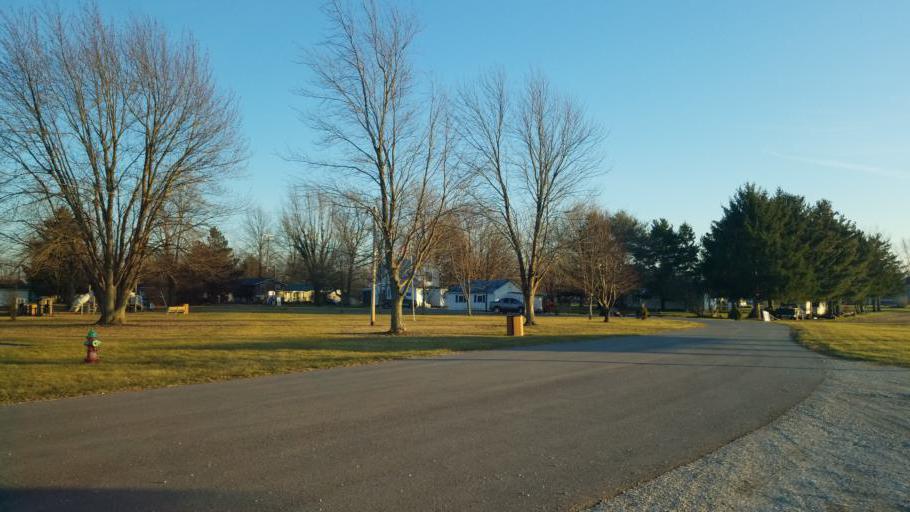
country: US
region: Ohio
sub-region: Wyandot County
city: Upper Sandusky
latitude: 40.8232
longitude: -83.1350
